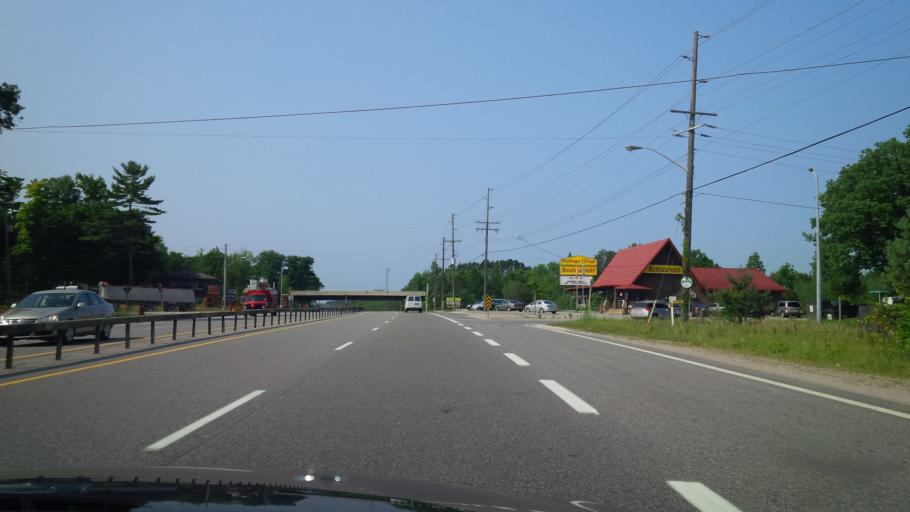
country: CA
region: Ontario
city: Orillia
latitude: 44.7251
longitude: -79.3740
